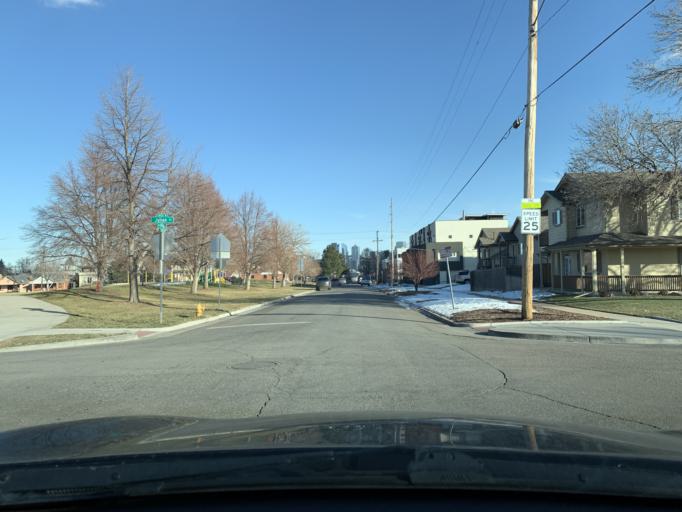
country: US
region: Colorado
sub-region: Jefferson County
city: Edgewater
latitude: 39.7464
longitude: -105.0316
